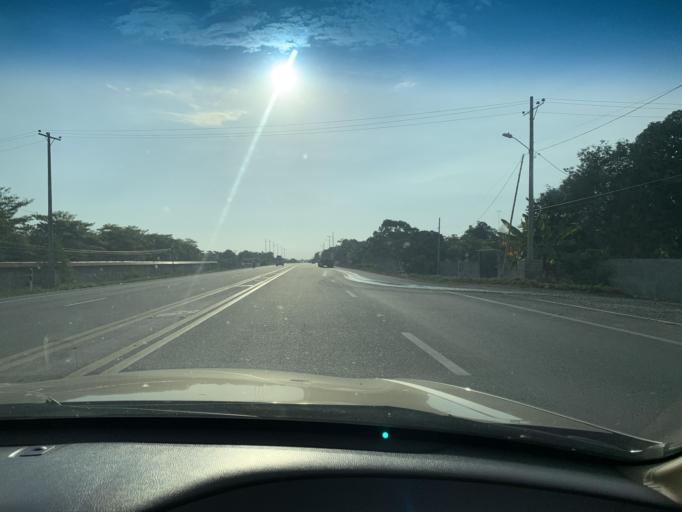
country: EC
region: Guayas
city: Naranjito
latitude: -2.2560
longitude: -79.5987
